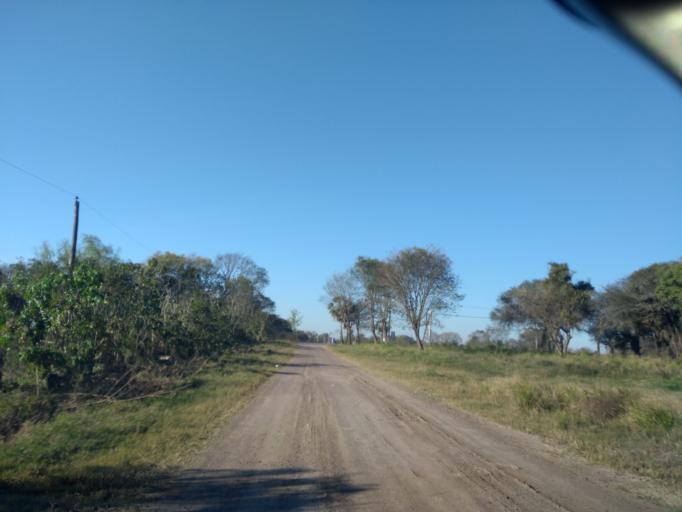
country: AR
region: Chaco
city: Barranqueras
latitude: -27.4368
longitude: -58.9279
